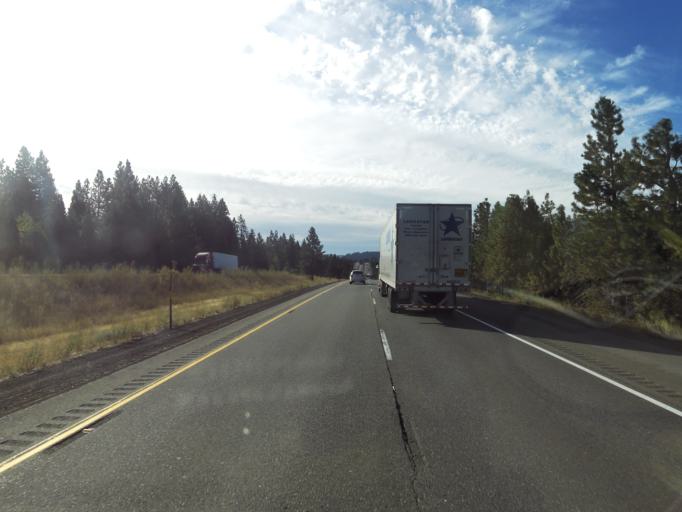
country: US
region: California
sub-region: Siskiyou County
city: Mount Shasta
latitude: 41.3042
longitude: -122.3171
